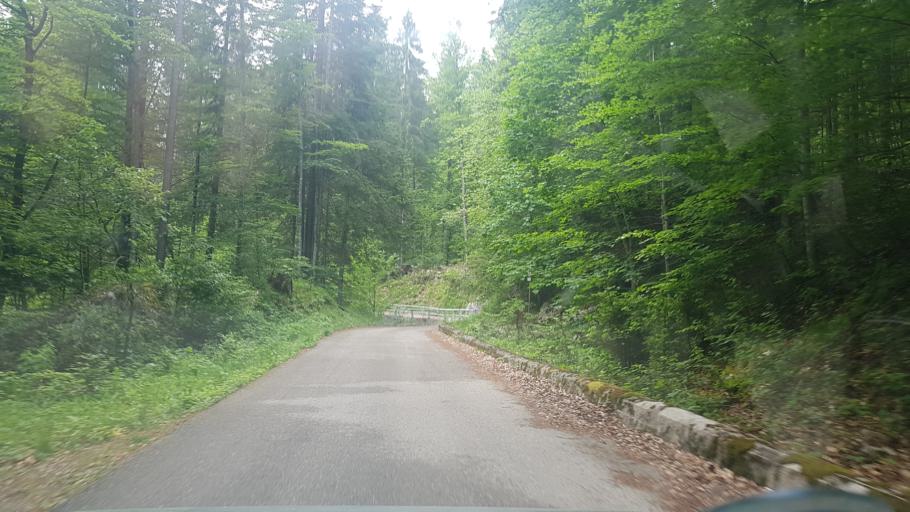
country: IT
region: Friuli Venezia Giulia
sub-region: Provincia di Udine
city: Paularo
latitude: 46.5359
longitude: 13.2077
